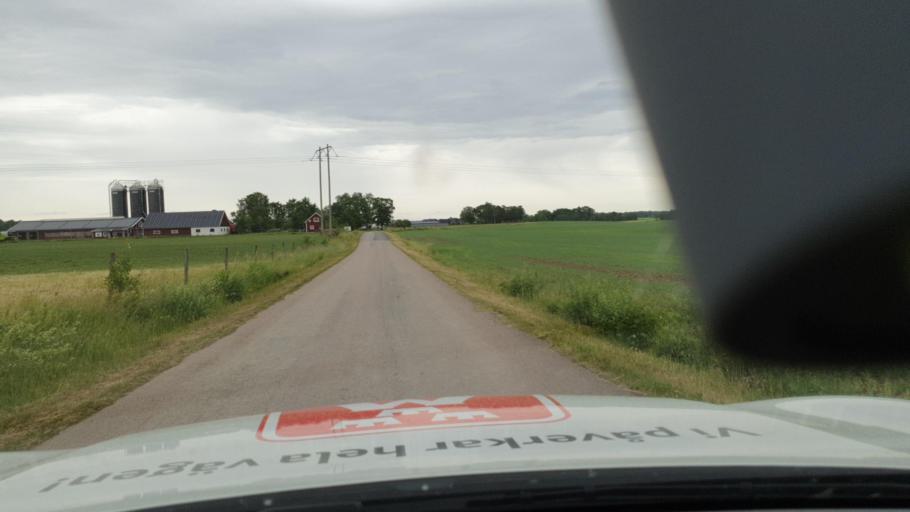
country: SE
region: Vaestra Goetaland
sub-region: Skovde Kommun
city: Skoevde
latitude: 58.3791
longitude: 13.8945
